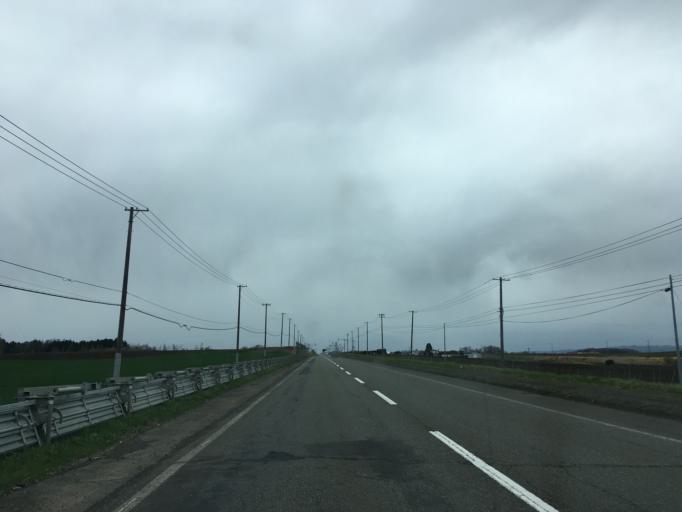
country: JP
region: Hokkaido
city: Chitose
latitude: 42.9217
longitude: 141.8090
